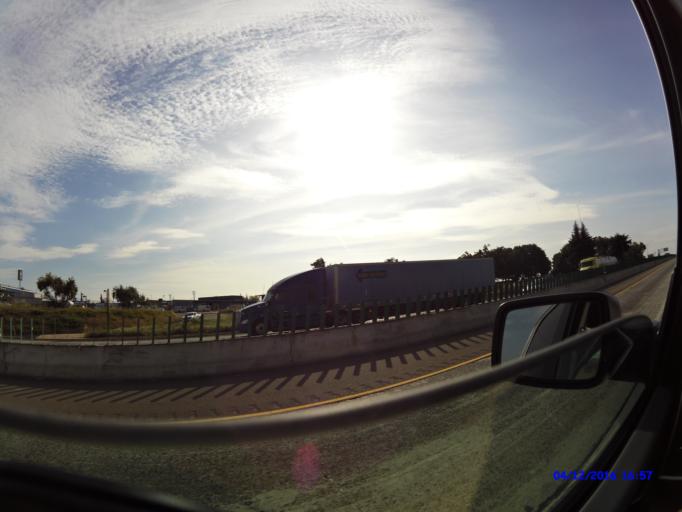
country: US
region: California
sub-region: Stanislaus County
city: Modesto
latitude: 37.6473
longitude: -121.0178
